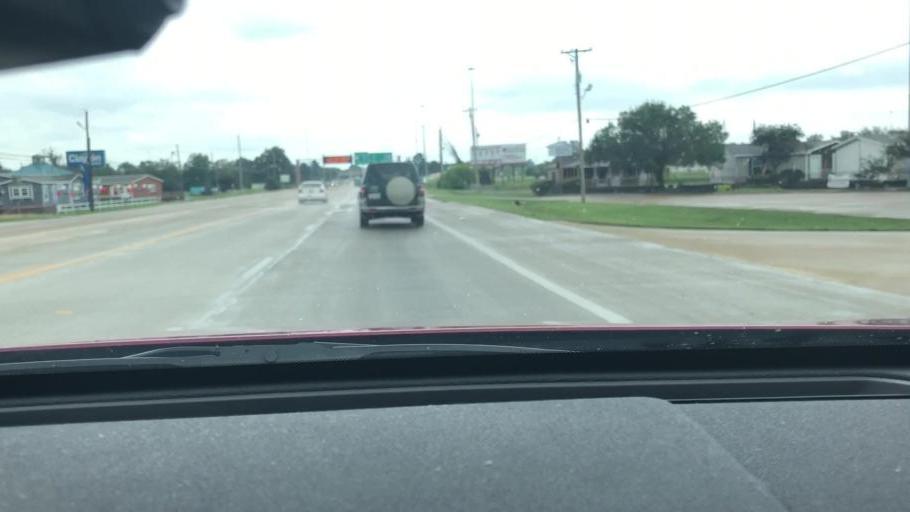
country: US
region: Texas
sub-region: Bowie County
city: Wake Village
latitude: 33.3898
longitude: -94.1063
